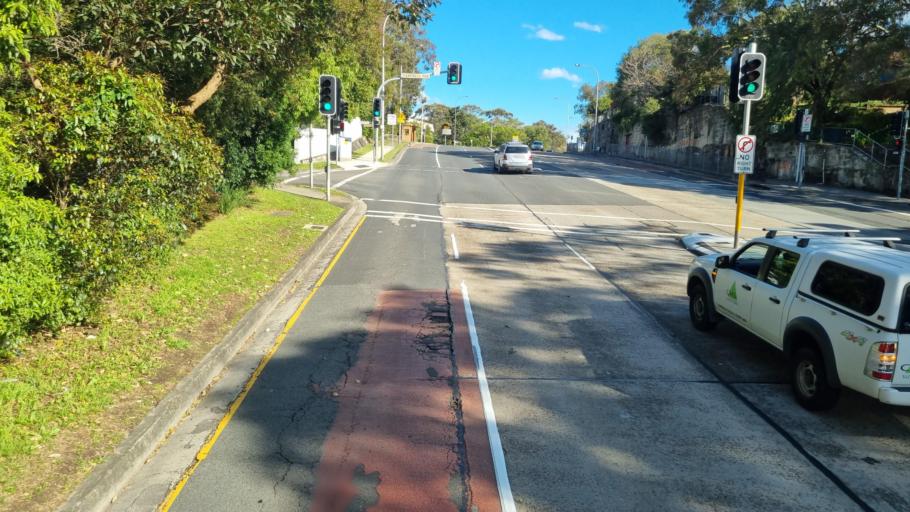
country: AU
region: New South Wales
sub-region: Warringah
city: North Manly
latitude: -33.7804
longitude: 151.2677
